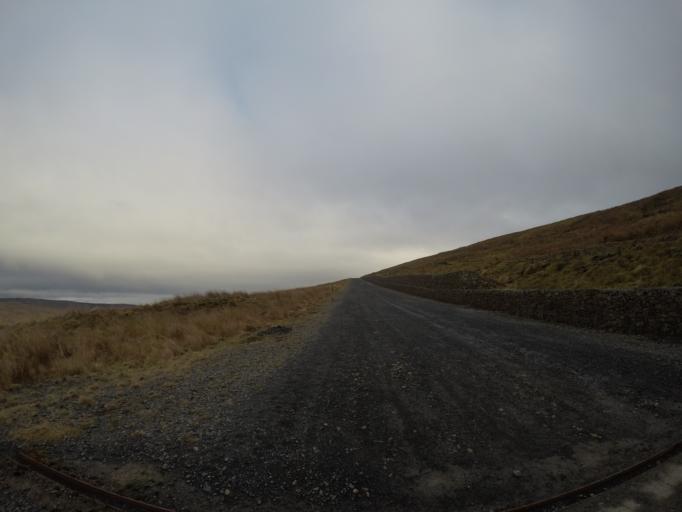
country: GB
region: Scotland
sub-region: North Ayrshire
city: Fairlie
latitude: 55.7638
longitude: -4.7966
